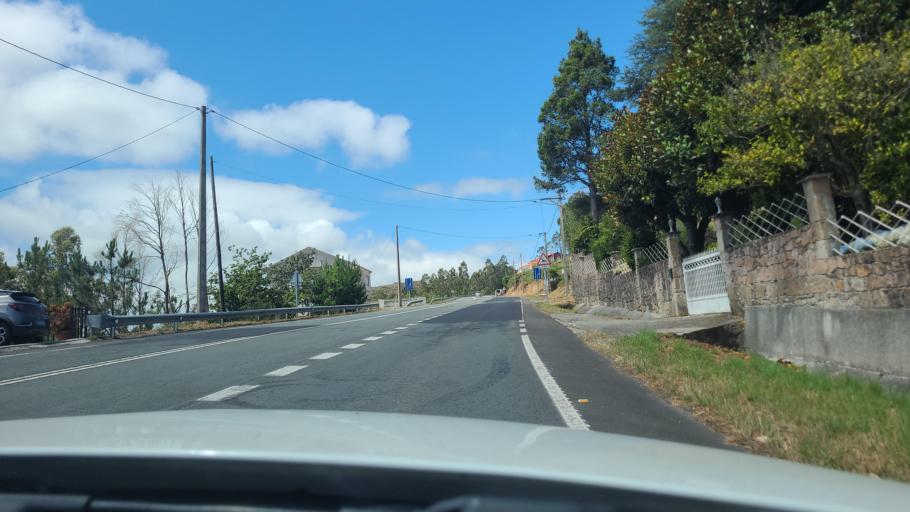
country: ES
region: Galicia
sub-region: Provincia da Coruna
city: Corcubion
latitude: 42.9110
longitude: -9.1435
